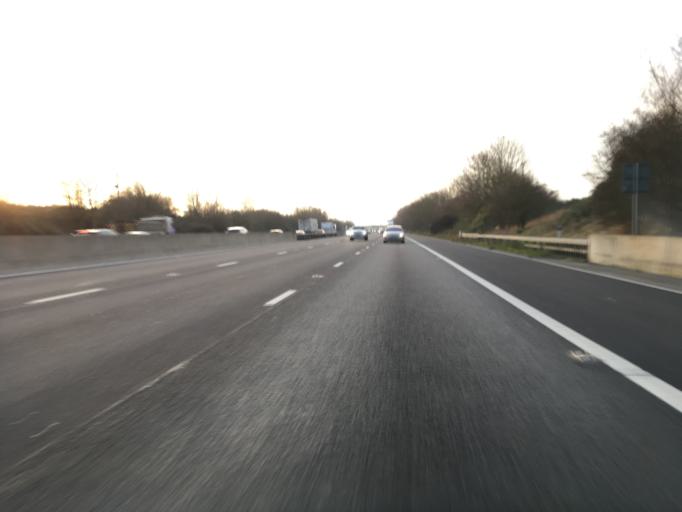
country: GB
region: England
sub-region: Gloucestershire
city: Uckington
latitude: 51.9563
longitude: -2.1279
